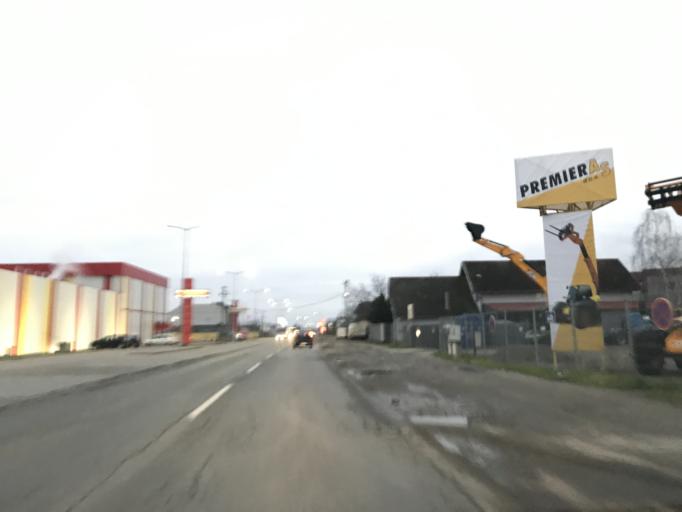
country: RS
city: Veternik
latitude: 45.2806
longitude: 19.7841
